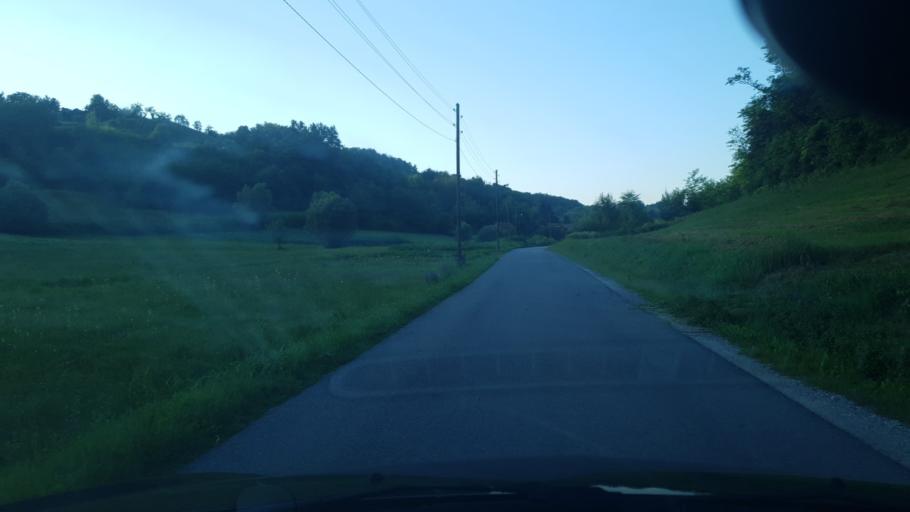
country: HR
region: Krapinsko-Zagorska
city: Zabok
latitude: 46.0514
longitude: 15.8875
